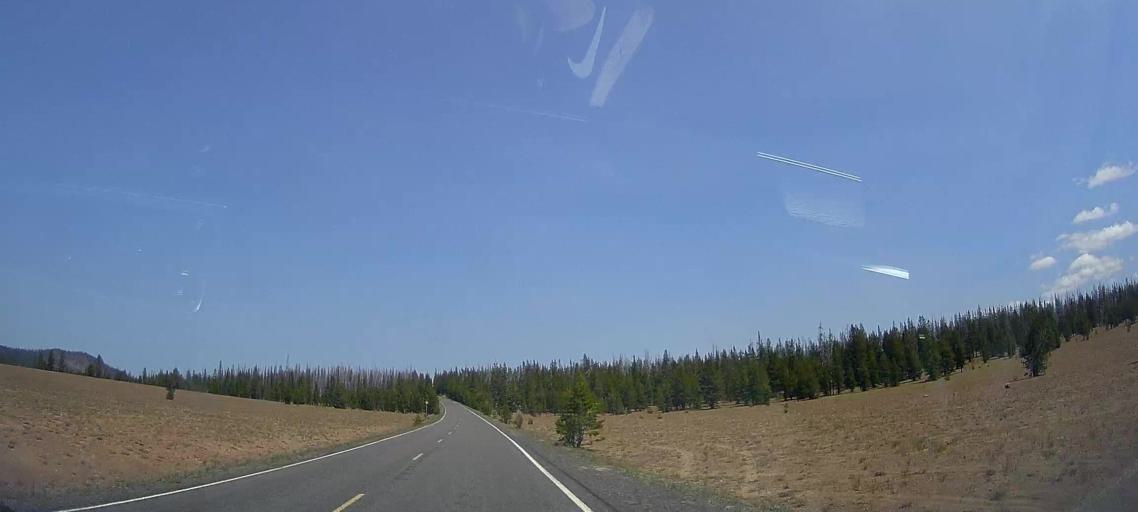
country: US
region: Oregon
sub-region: Lane County
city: Oakridge
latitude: 43.0337
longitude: -122.1174
